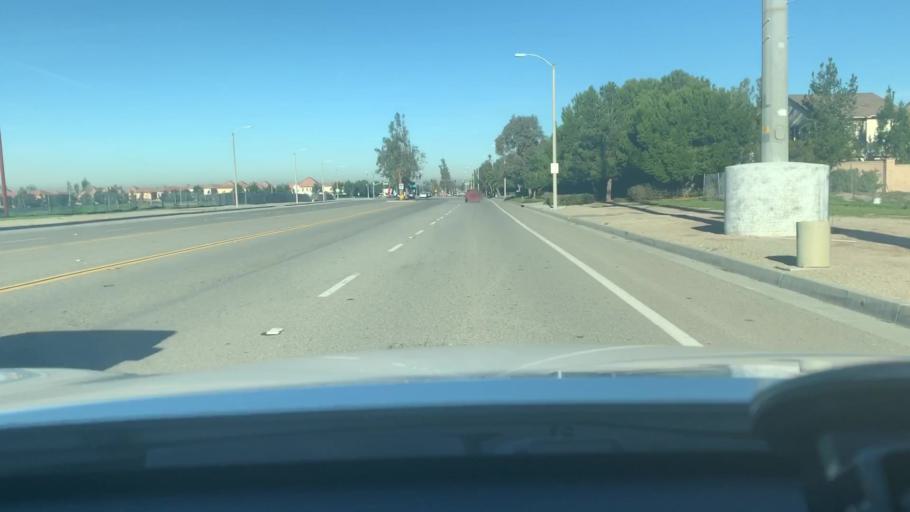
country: US
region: California
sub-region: Orange County
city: Lake Forest
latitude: 33.6854
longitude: -117.7463
